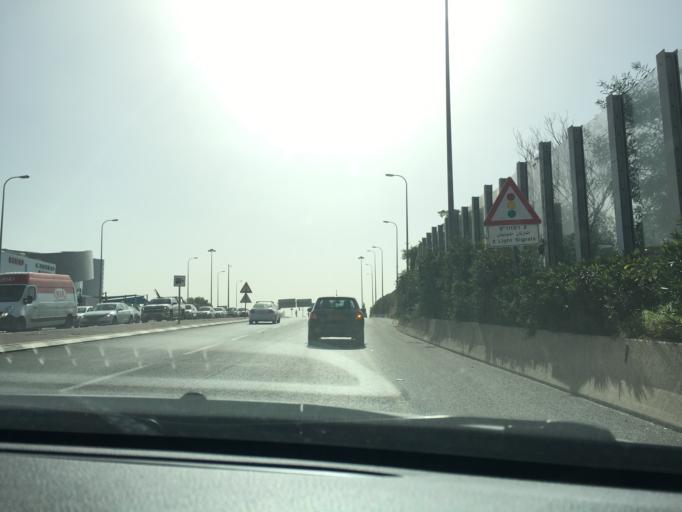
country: IL
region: Central District
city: Kfar Saba
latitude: 32.1667
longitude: 34.9273
